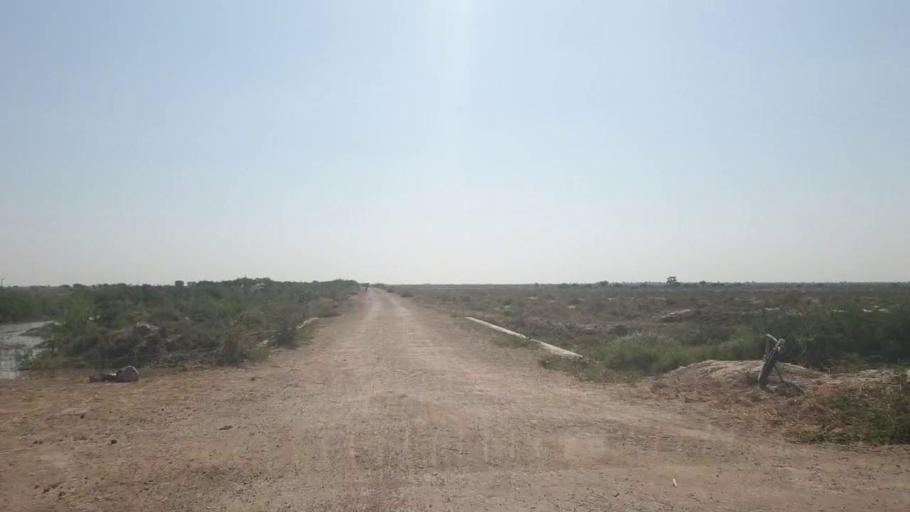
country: PK
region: Sindh
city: Tando Bago
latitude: 24.8771
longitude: 69.1643
